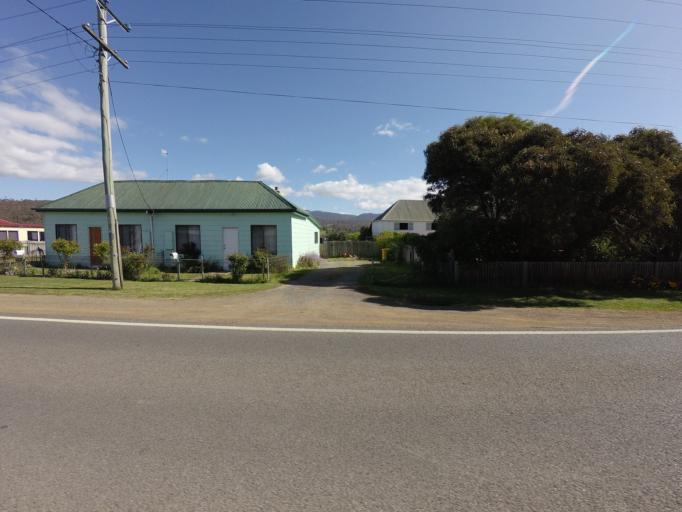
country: AU
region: Tasmania
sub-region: Derwent Valley
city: New Norfolk
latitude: -42.7706
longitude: 147.0313
